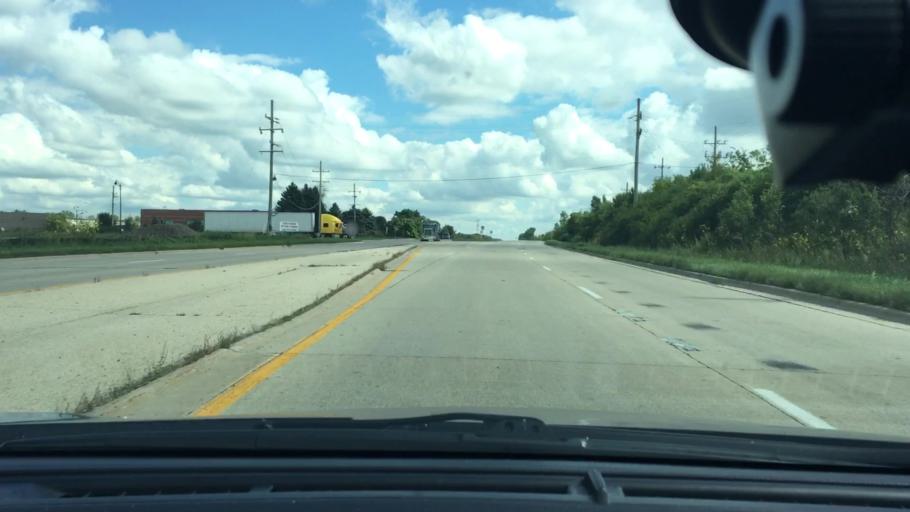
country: US
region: Illinois
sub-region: Kane County
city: East Dundee
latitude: 42.0911
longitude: -88.2522
